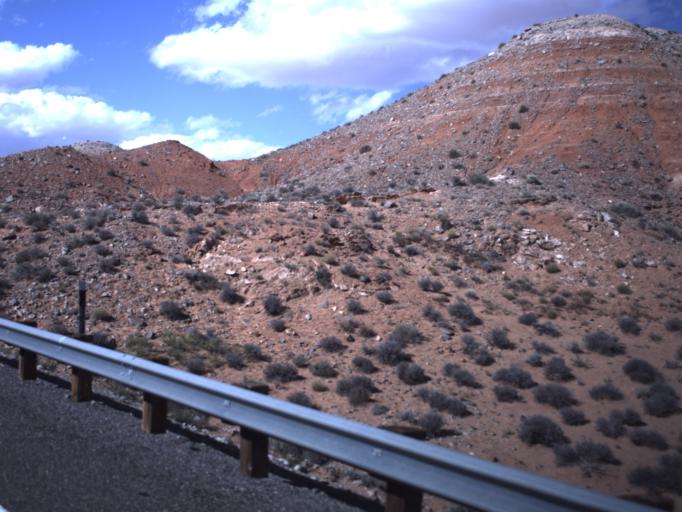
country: US
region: Utah
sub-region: Wayne County
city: Loa
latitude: 38.1430
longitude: -110.6110
